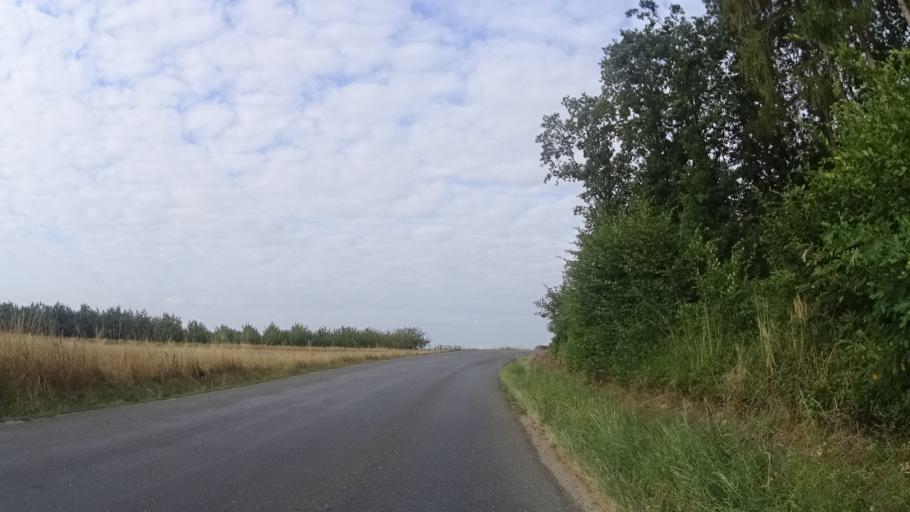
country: CZ
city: Stezery
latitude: 50.2083
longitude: 15.7194
